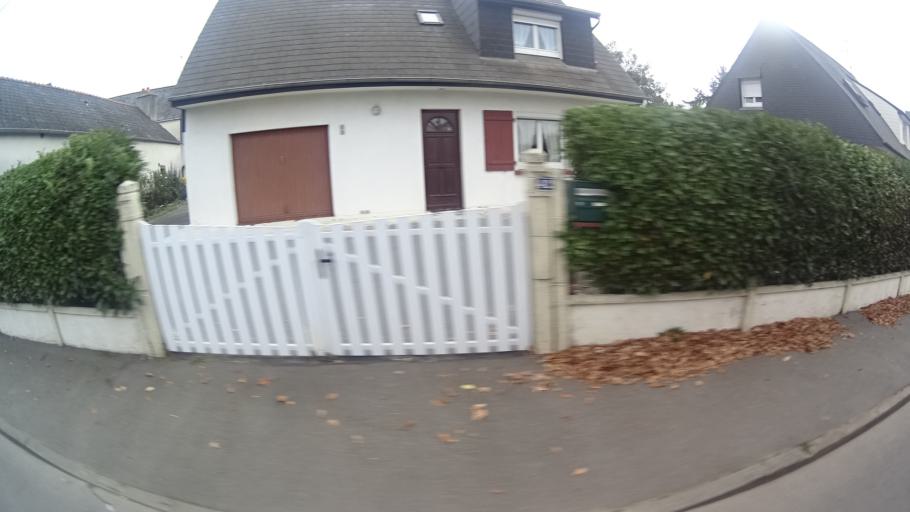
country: FR
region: Brittany
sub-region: Departement d'Ille-et-Vilaine
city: Redon
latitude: 47.6622
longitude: -2.0716
